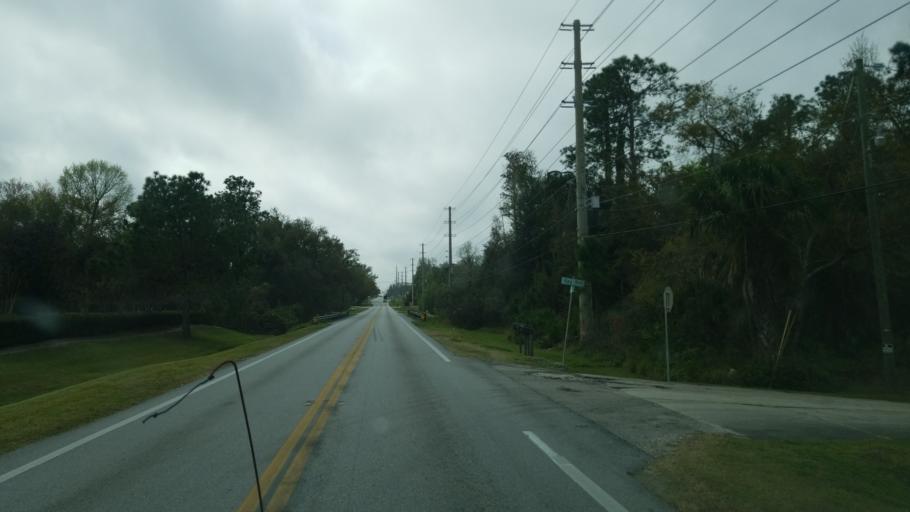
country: US
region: Florida
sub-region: Polk County
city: Kathleen
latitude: 28.0852
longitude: -82.0068
